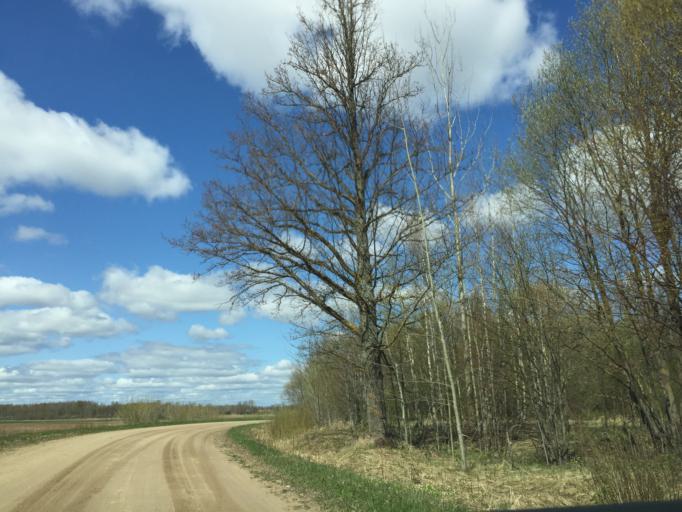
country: LV
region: Vilanu
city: Vilani
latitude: 56.6648
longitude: 27.1054
